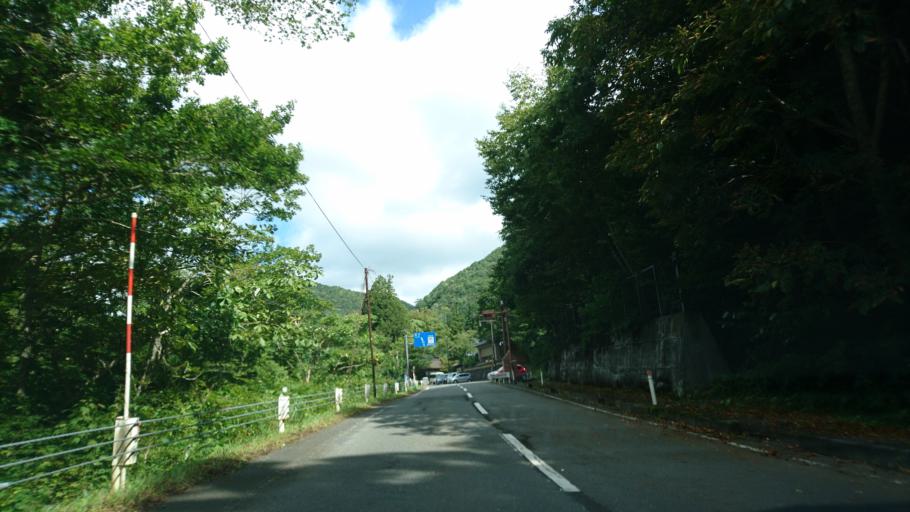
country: JP
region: Miyagi
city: Furukawa
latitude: 38.8601
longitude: 140.7777
